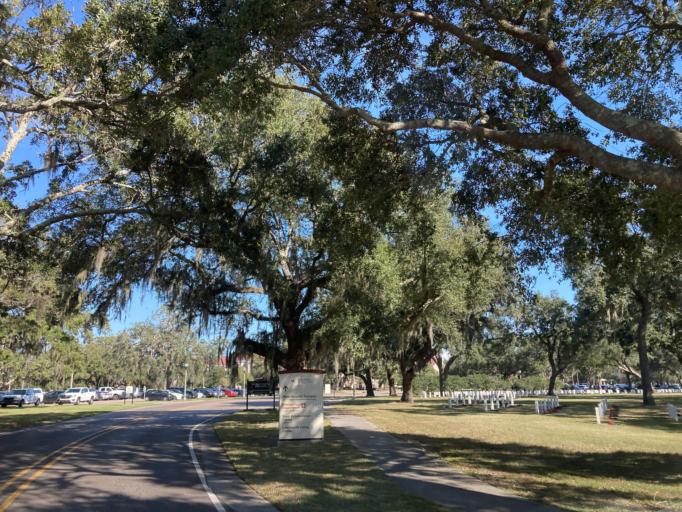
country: US
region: Mississippi
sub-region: Harrison County
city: D'Iberville
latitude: 30.4120
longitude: -88.9466
